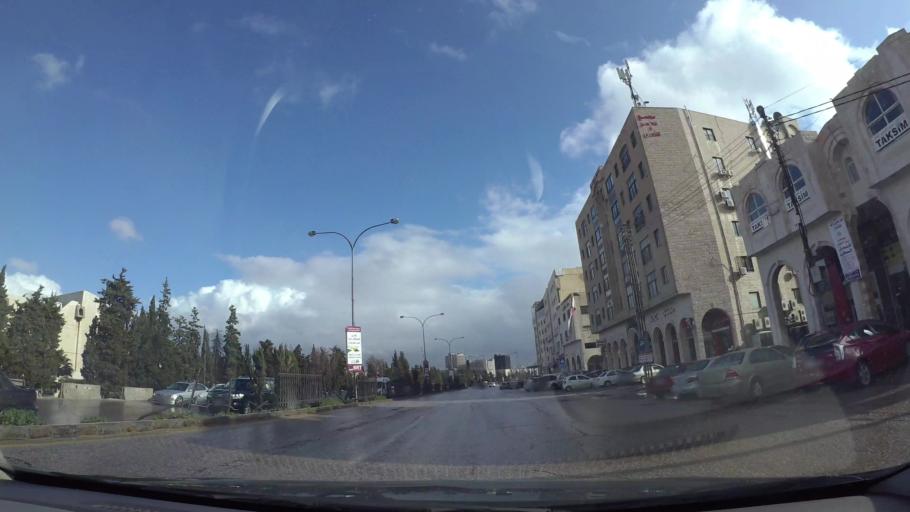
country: JO
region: Amman
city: Al Jubayhah
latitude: 32.0140
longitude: 35.8690
